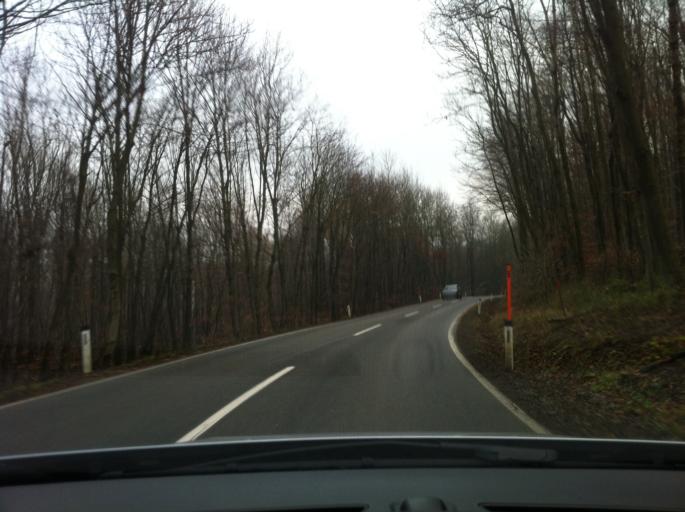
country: AT
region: Lower Austria
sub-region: Politischer Bezirk Wien-Umgebung
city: Mauerbach
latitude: 48.2500
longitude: 16.2456
